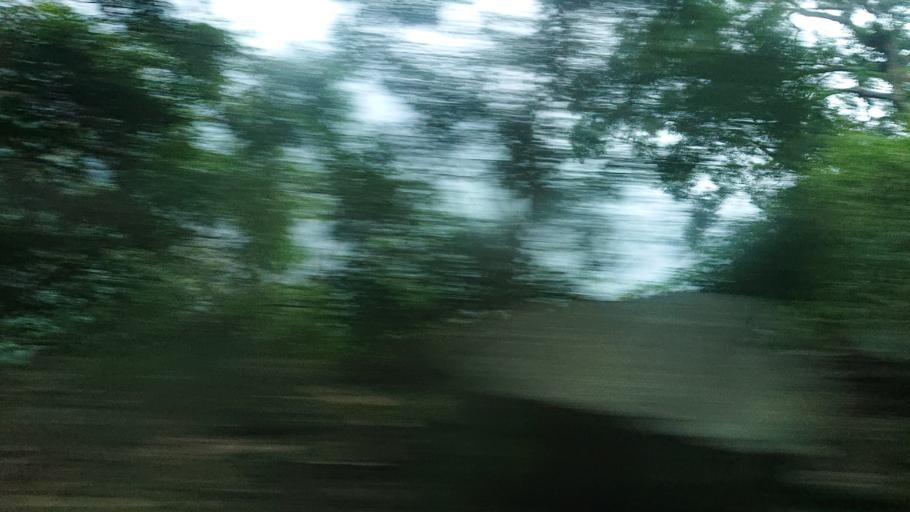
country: TW
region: Taiwan
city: Lugu
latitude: 23.5953
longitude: 120.7180
